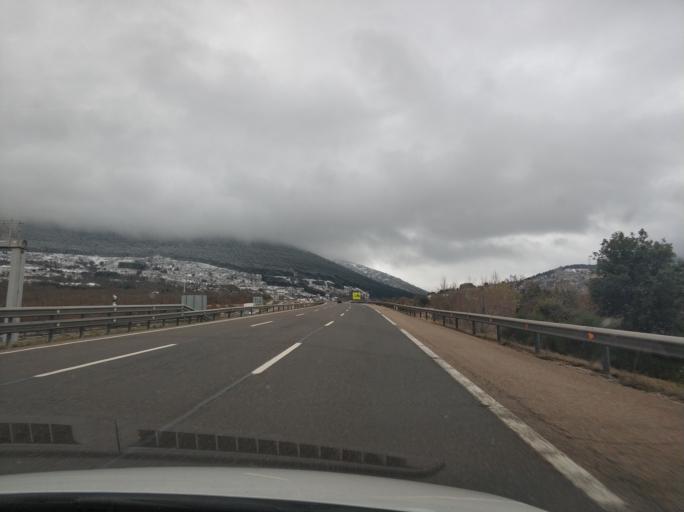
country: ES
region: Castille and Leon
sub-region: Provincia de Segovia
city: Cerezo de Abajo
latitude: 41.1820
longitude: -3.5845
